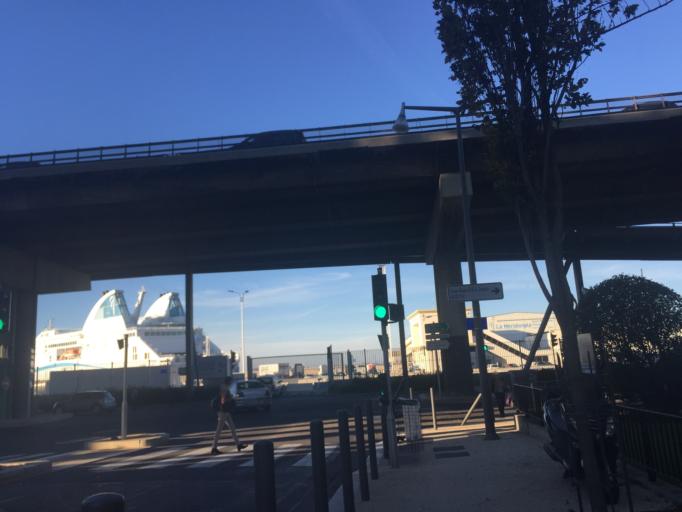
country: FR
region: Provence-Alpes-Cote d'Azur
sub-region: Departement des Bouches-du-Rhone
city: Marseille 03
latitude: 43.3134
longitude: 5.3667
